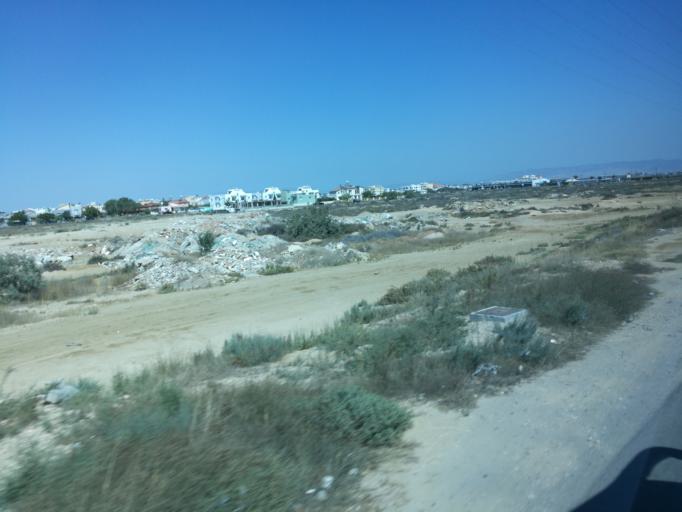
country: CY
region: Ammochostos
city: Famagusta
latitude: 35.1560
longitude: 33.9005
